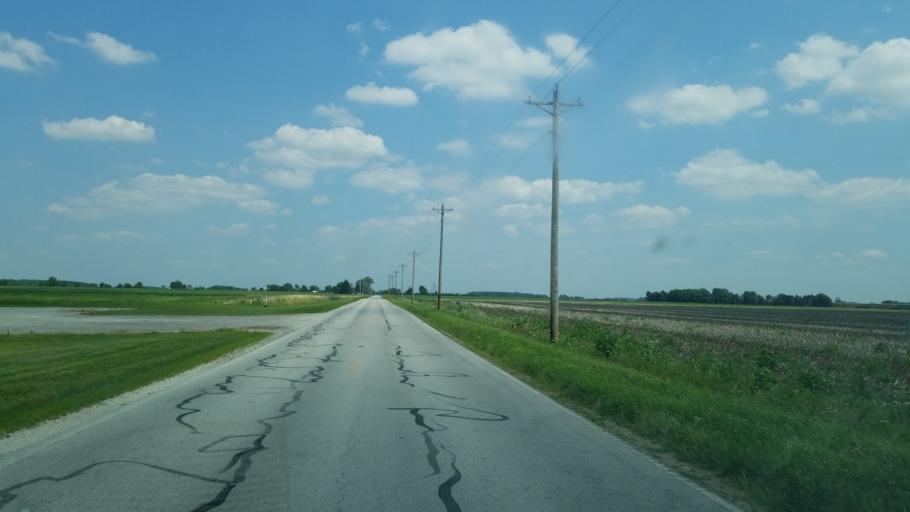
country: US
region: Ohio
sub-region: Seneca County
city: Fostoria
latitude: 41.1815
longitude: -83.3552
